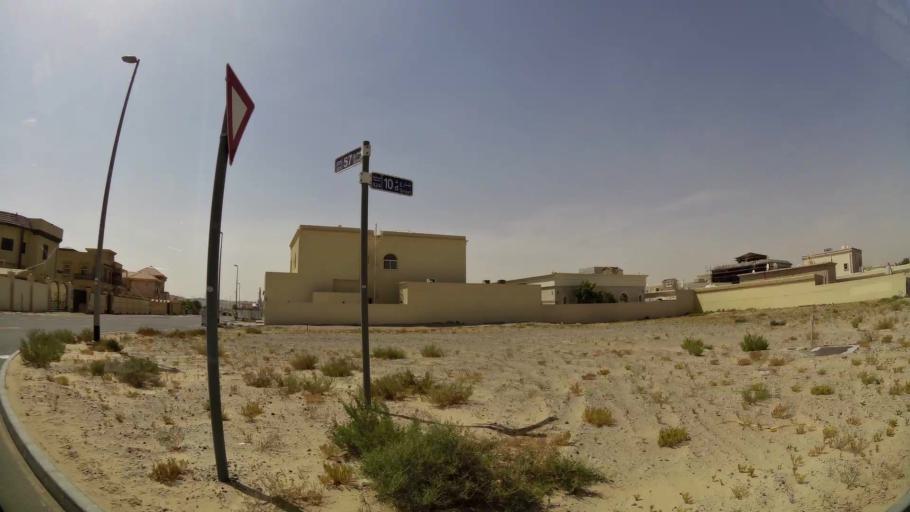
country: AE
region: Ash Shariqah
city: Sharjah
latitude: 25.1896
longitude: 55.4341
